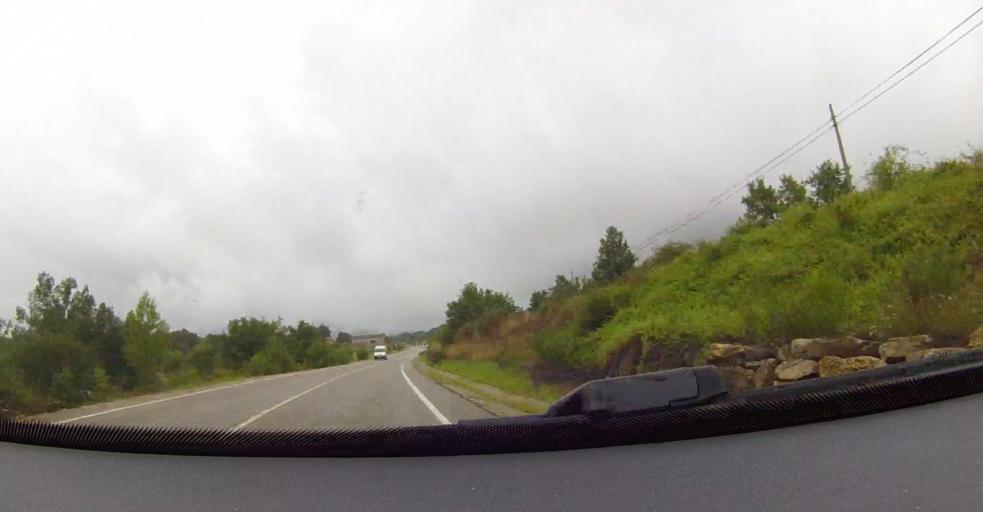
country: ES
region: Castille and Leon
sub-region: Provincia de Leon
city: Bonar
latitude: 42.8474
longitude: -5.2717
